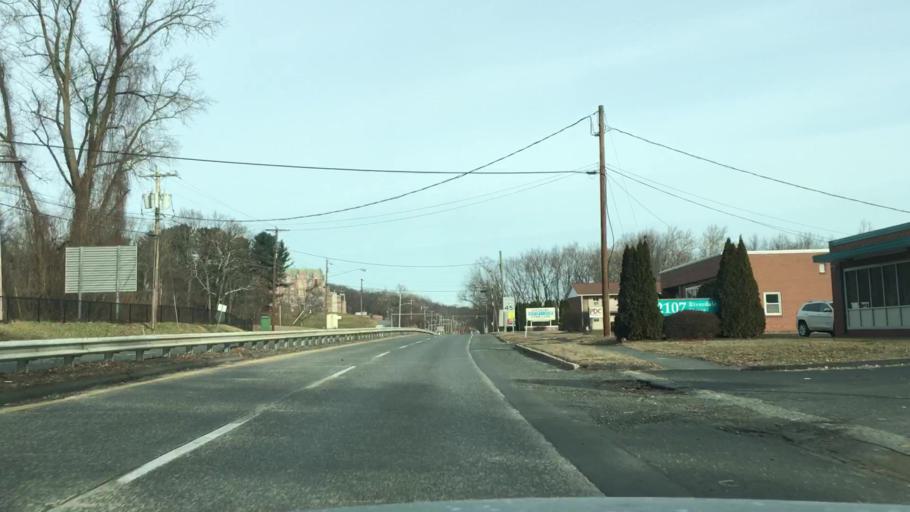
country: US
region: Massachusetts
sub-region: Hampden County
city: Chicopee
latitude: 42.1604
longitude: -72.6331
